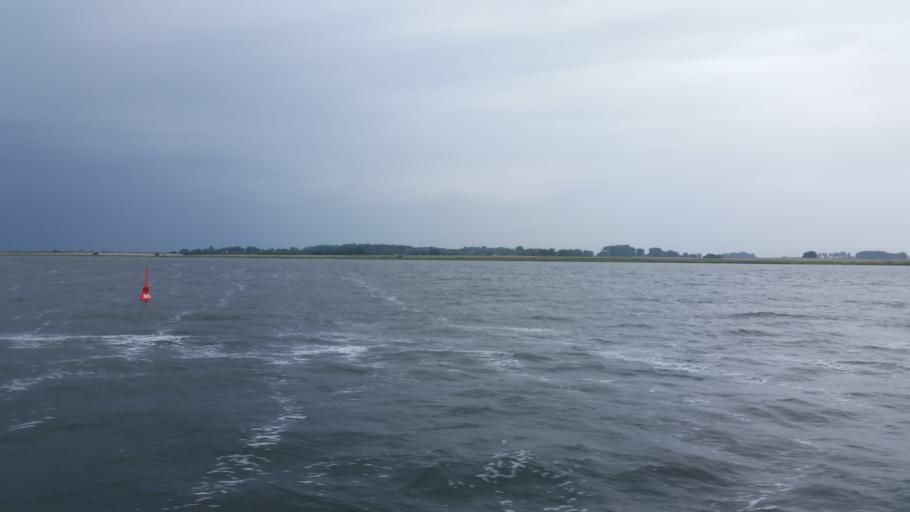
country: DE
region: Mecklenburg-Vorpommern
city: Hiddensee
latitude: 54.5190
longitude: 13.1564
